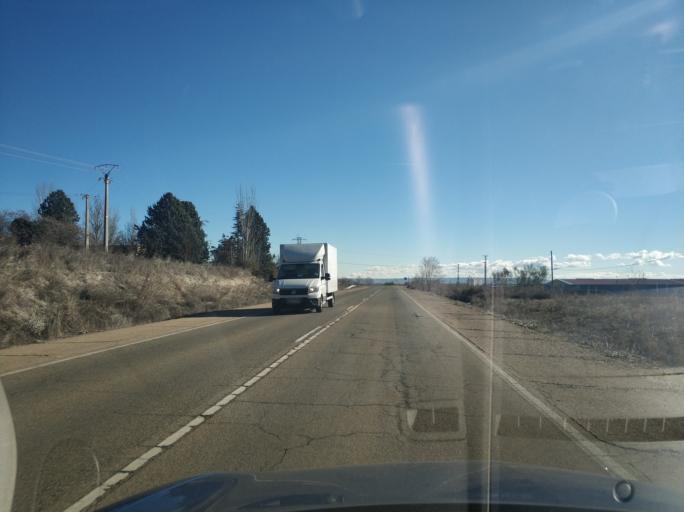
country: ES
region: Castille and Leon
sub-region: Provincia de Valladolid
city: Cisterniga
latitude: 41.6021
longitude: -4.6729
